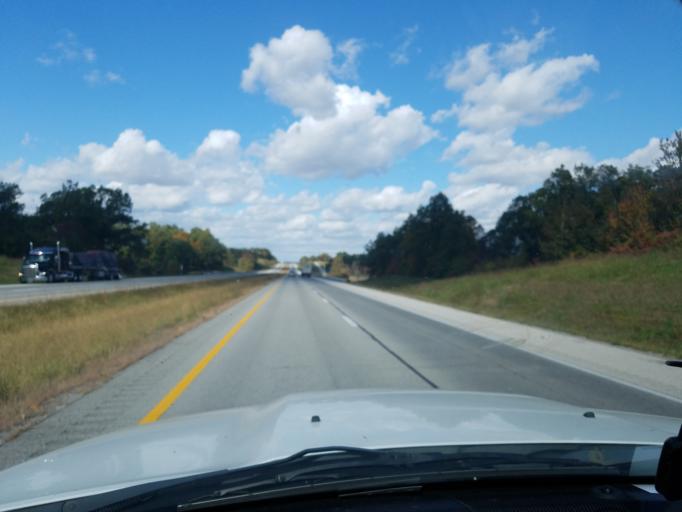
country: US
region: Kentucky
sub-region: Daviess County
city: Masonville
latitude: 37.6250
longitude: -86.9877
